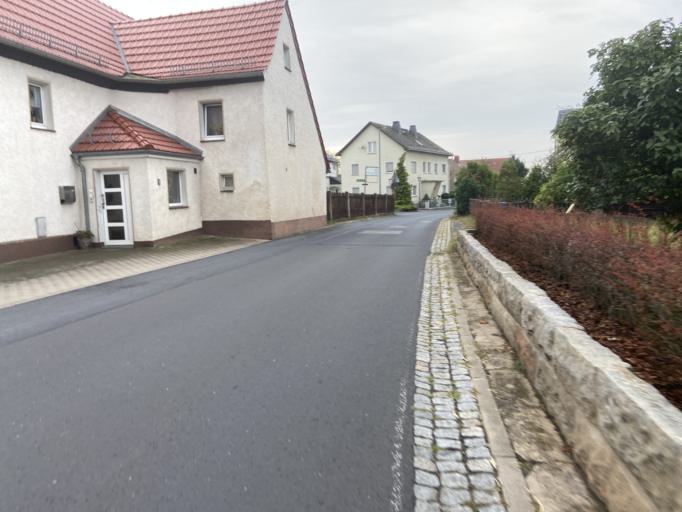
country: DE
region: Saxony
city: Tharandt
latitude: 51.0159
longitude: 13.5731
